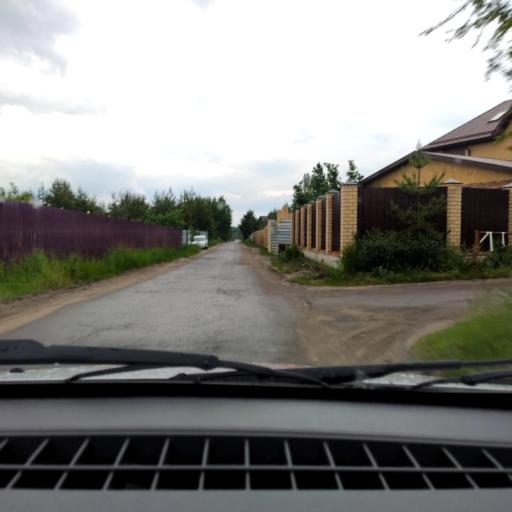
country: RU
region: Voronezj
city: Ramon'
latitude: 51.8545
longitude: 39.2437
